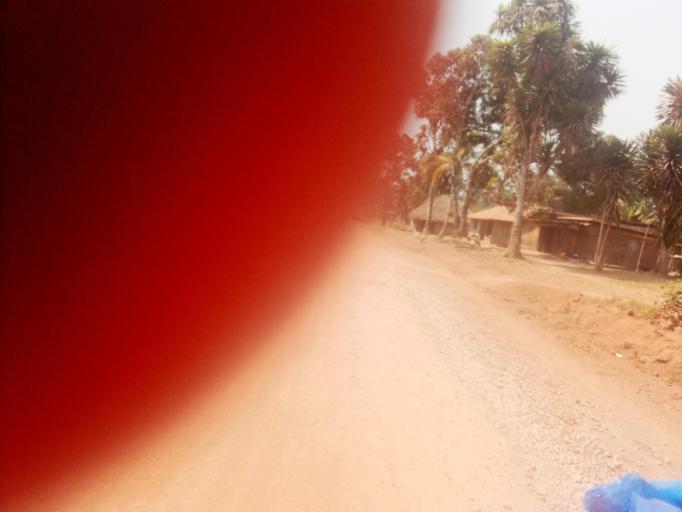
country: SL
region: Southern Province
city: Sumbuya
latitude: 7.6592
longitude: -11.9949
